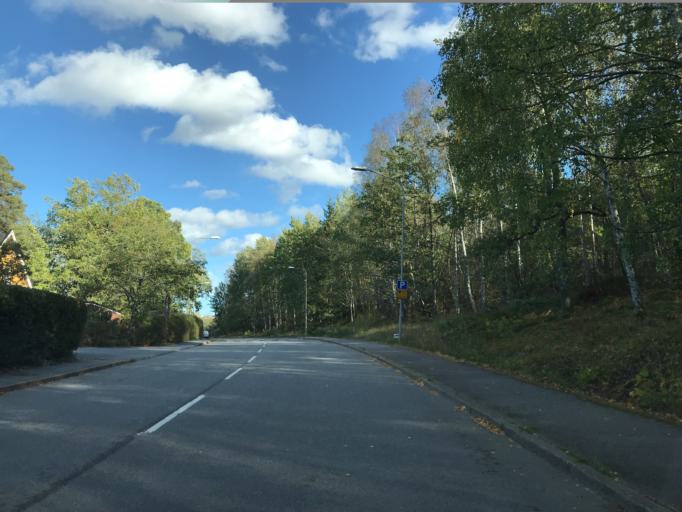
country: SE
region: Stockholm
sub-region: Huddinge Kommun
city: Segeltorp
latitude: 59.2854
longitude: 17.9033
